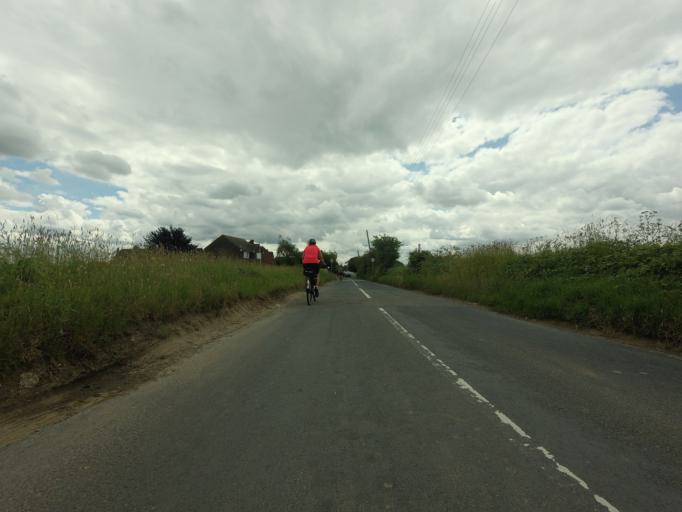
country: GB
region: England
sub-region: Medway
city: Allhallows
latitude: 51.4577
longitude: 0.6374
